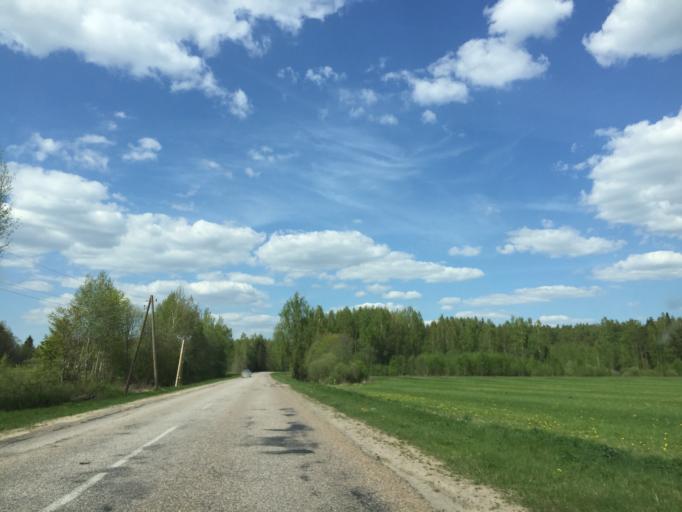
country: LV
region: Limbazu Rajons
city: Limbazi
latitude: 57.4023
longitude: 24.6910
